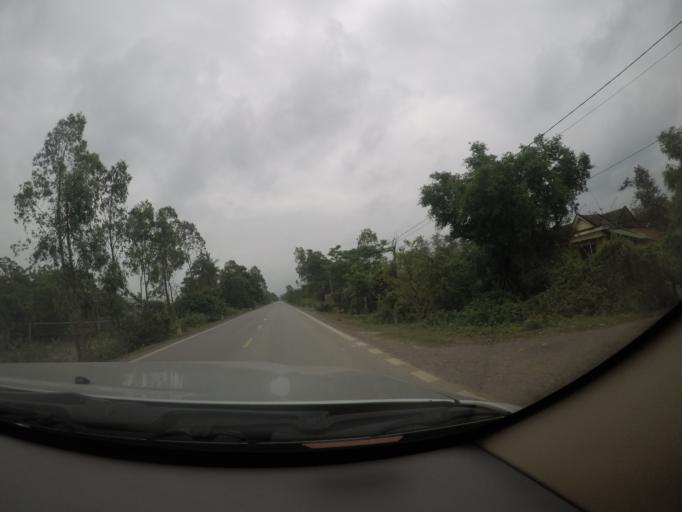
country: VN
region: Quang Binh
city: Quan Hau
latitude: 17.3024
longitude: 106.6407
